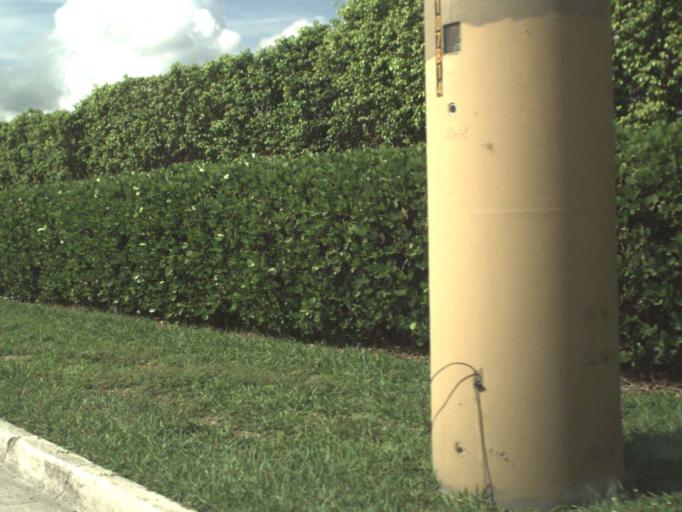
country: US
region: Florida
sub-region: Miami-Dade County
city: Ojus
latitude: 25.9532
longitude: -80.1469
